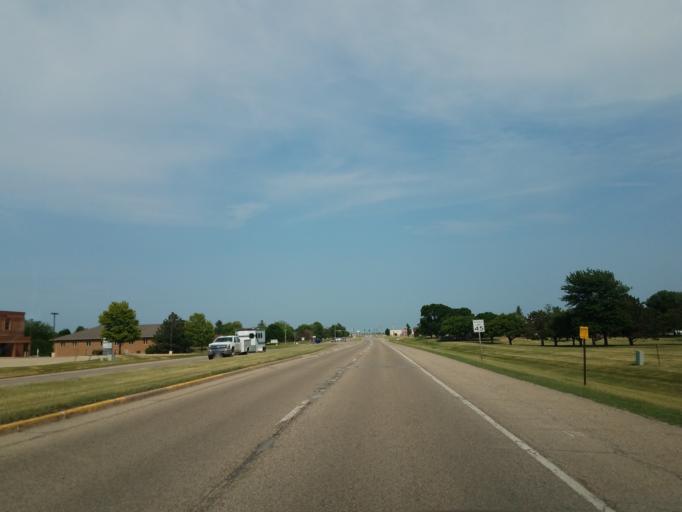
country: US
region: Illinois
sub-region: McLean County
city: Bloomington
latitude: 40.4883
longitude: -88.9333
